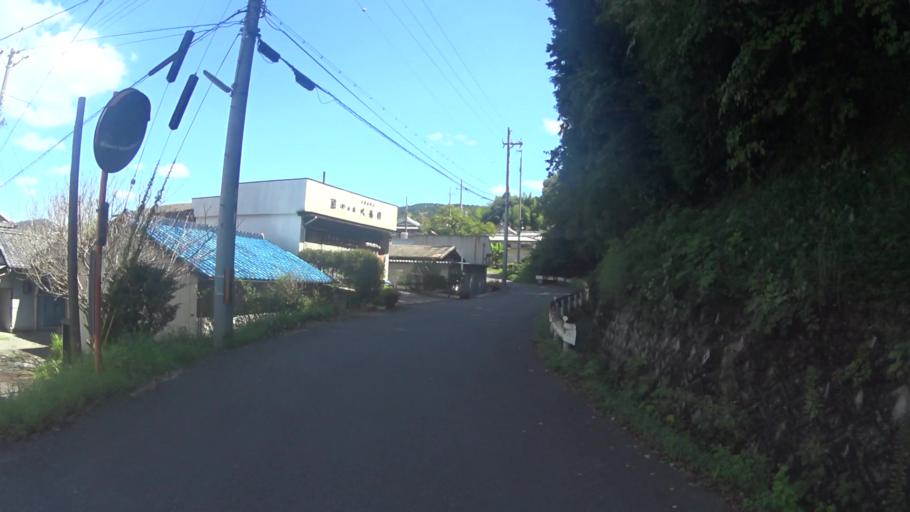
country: JP
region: Nara
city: Nara-shi
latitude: 34.7472
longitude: 135.8693
